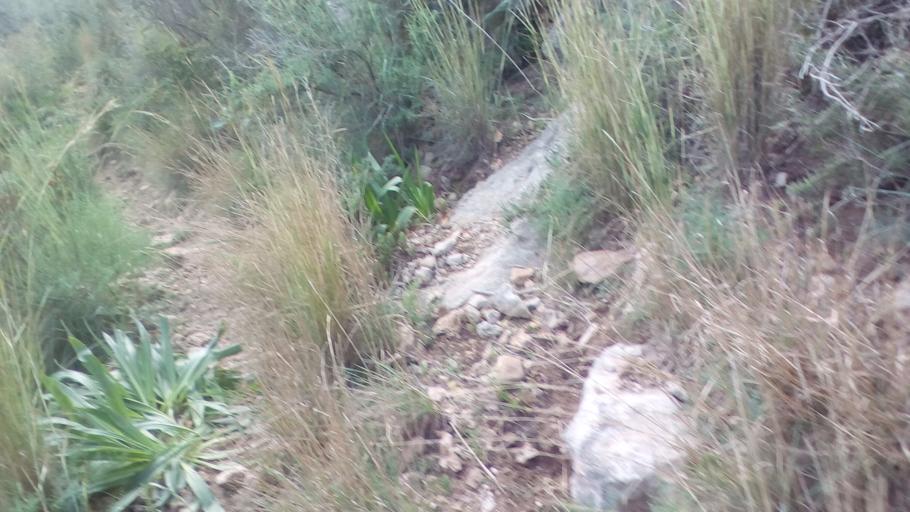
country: ES
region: Valencia
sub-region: Provincia de Valencia
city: Xeraco,Jaraco
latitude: 39.0527
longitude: -0.2300
